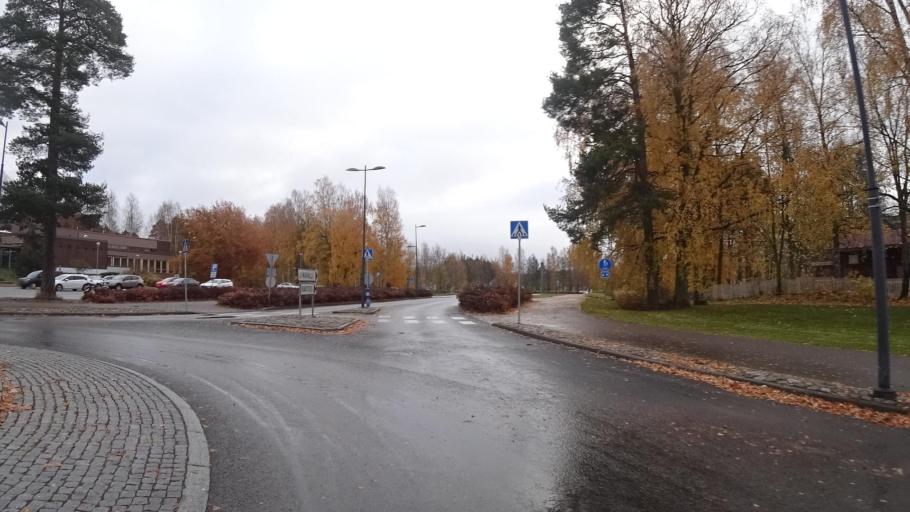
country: FI
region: Northern Savo
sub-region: Varkaus
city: Varkaus
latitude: 62.3123
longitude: 27.8883
